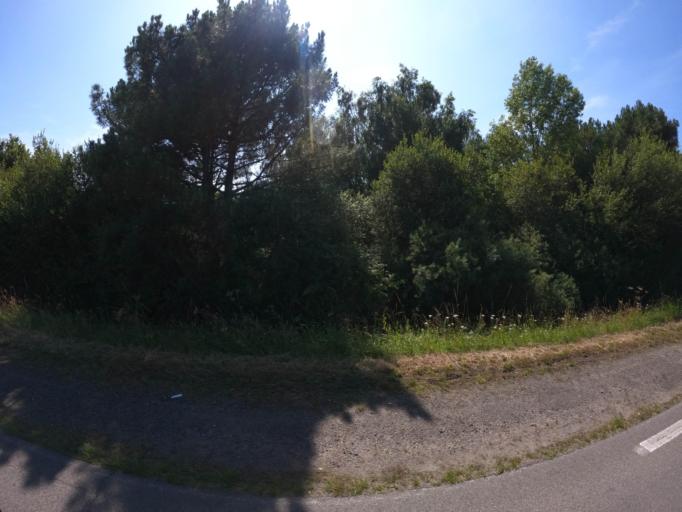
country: FR
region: Pays de la Loire
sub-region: Departement de la Loire-Atlantique
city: La Bernerie-en-Retz
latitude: 47.0938
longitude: -2.0351
